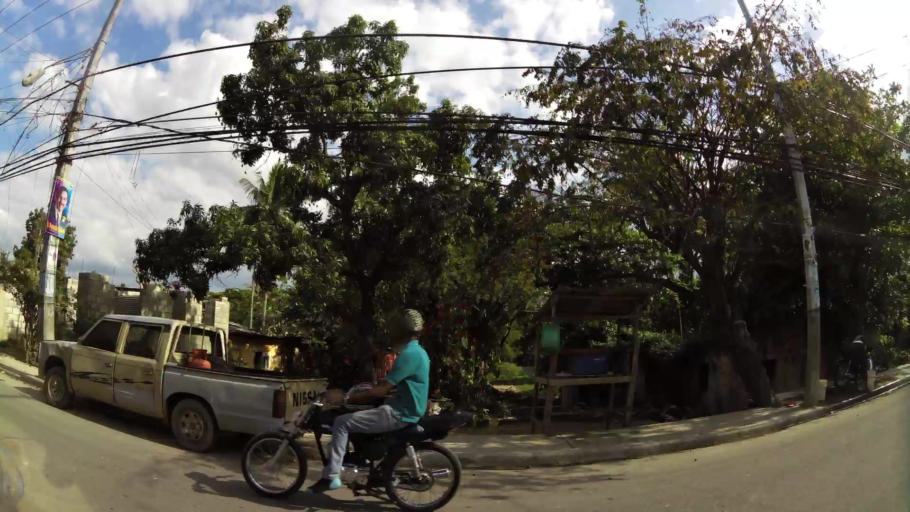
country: DO
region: Nacional
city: Ensanche Luperon
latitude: 18.5444
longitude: -69.8899
